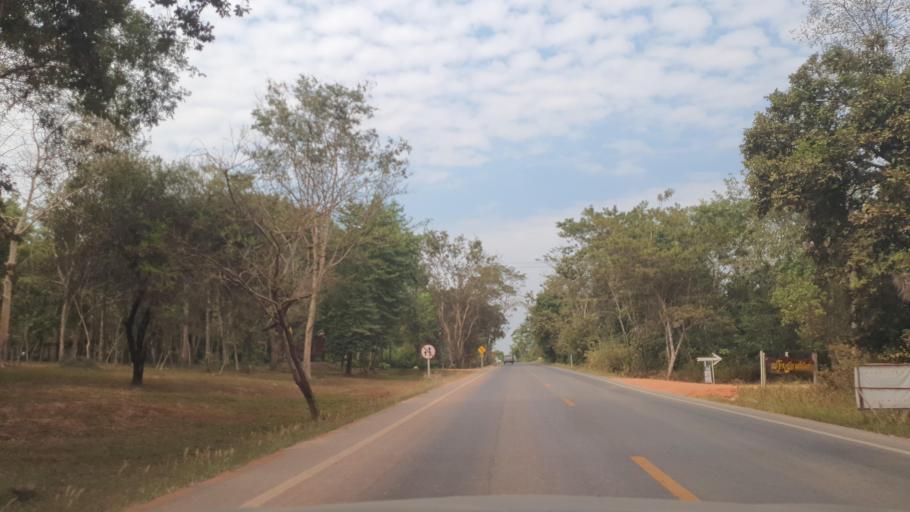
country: TH
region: Changwat Bueng Kan
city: Bung Khla
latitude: 18.2884
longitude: 103.8926
